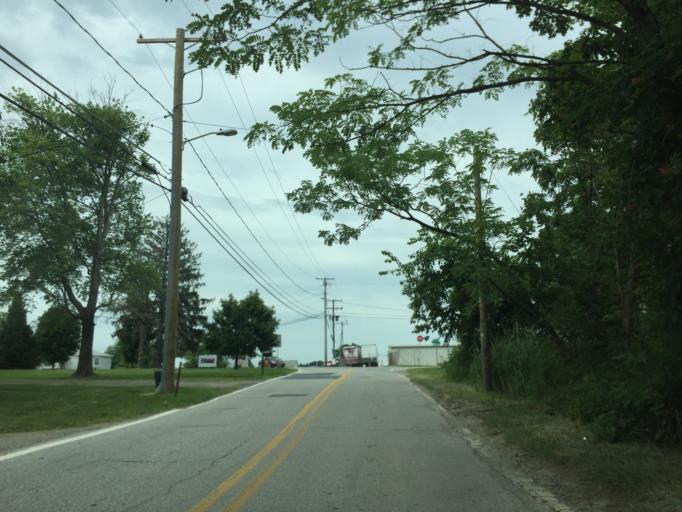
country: US
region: Maryland
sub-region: Baltimore County
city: Essex
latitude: 39.2799
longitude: -76.4676
